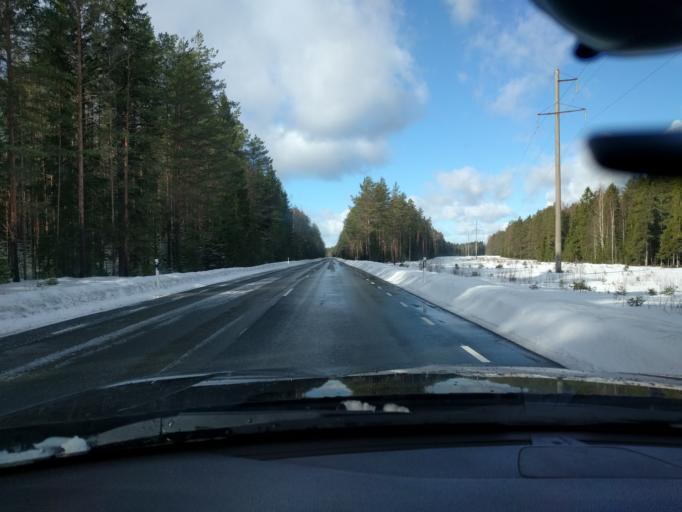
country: EE
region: Harju
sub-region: Kuusalu vald
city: Kuusalu
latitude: 59.2074
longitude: 25.5594
